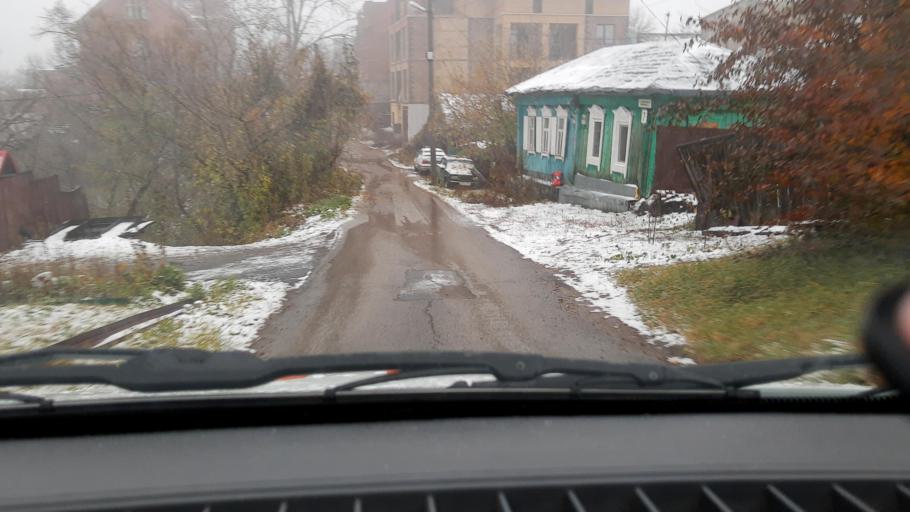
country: RU
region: Bashkortostan
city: Ufa
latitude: 54.7209
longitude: 55.9220
